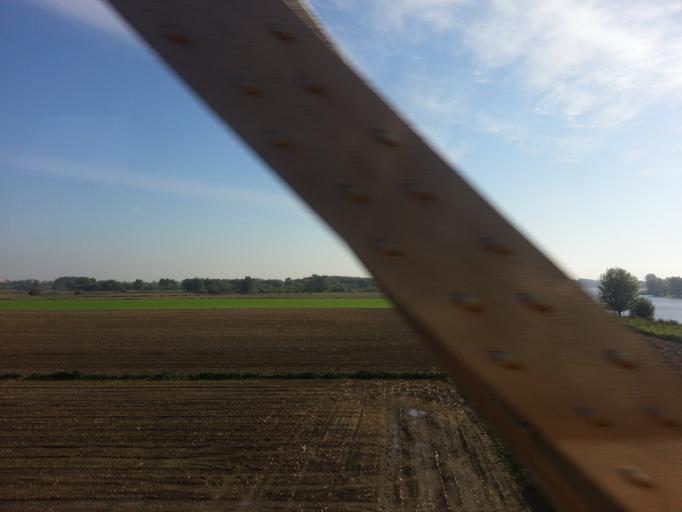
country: NL
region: Gelderland
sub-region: Gemeente Maasdriel
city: Hedel
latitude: 51.7415
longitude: 5.2741
